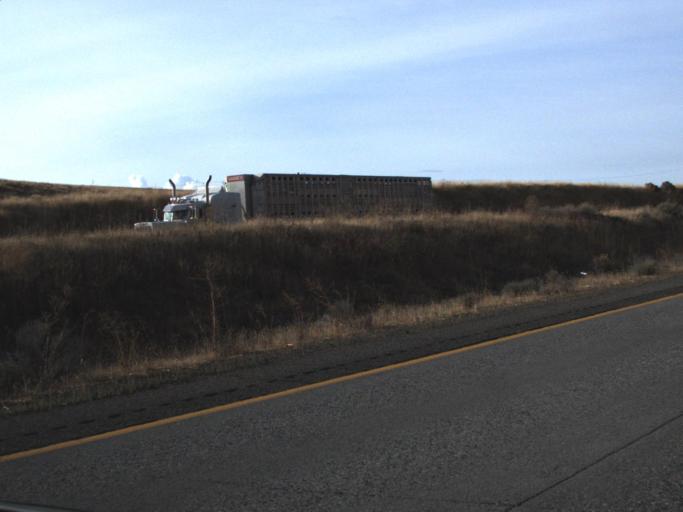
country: US
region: Washington
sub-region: Benton County
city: Highland
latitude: 46.0651
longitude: -119.2233
